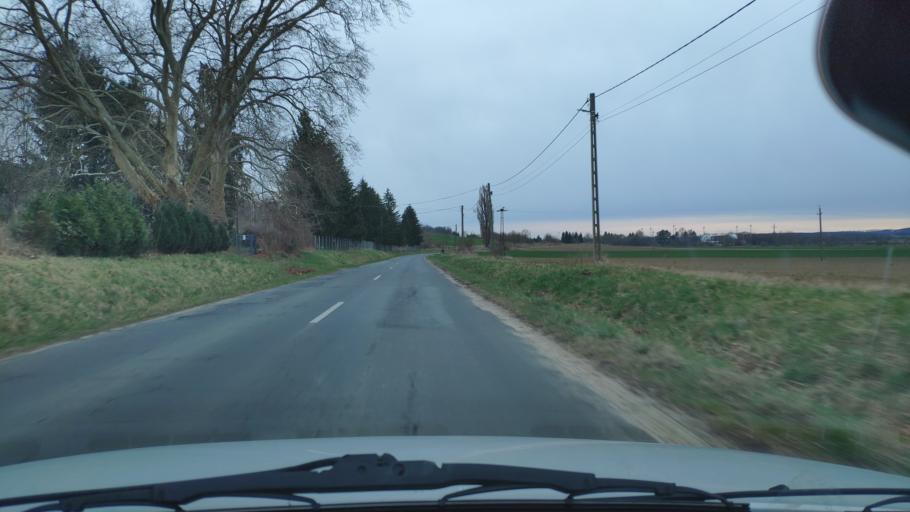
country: HU
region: Zala
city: Nagykanizsa
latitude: 46.5540
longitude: 16.9895
